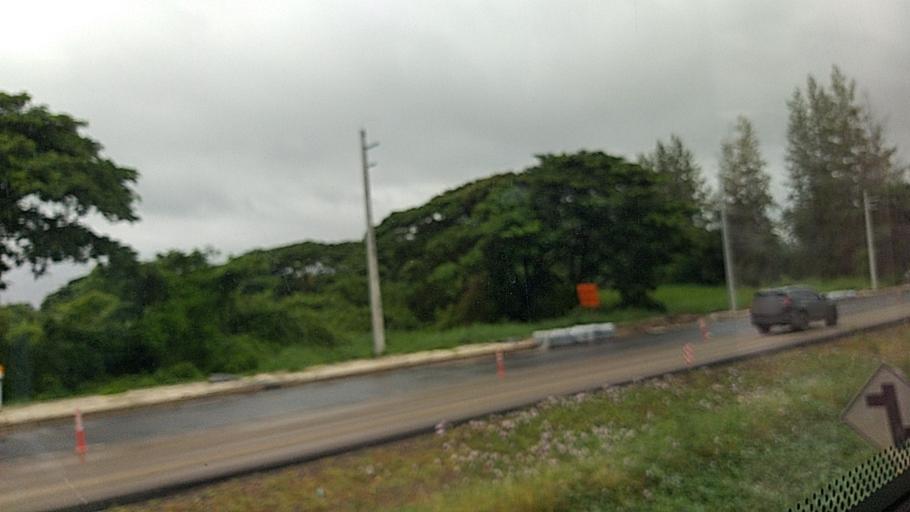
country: TH
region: Nakhon Ratchasima
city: Nakhon Ratchasima
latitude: 14.9928
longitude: 102.0635
